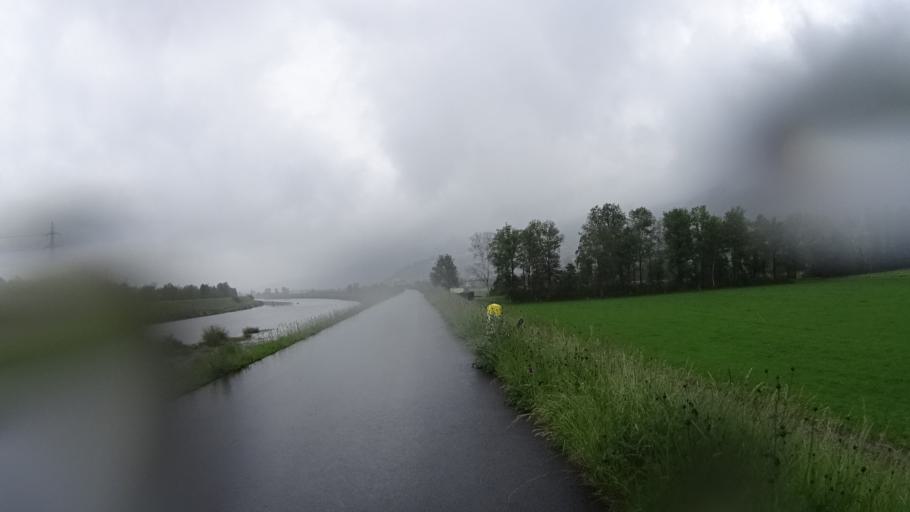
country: LI
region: Triesen
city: Triesen
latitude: 47.0928
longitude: 9.5189
